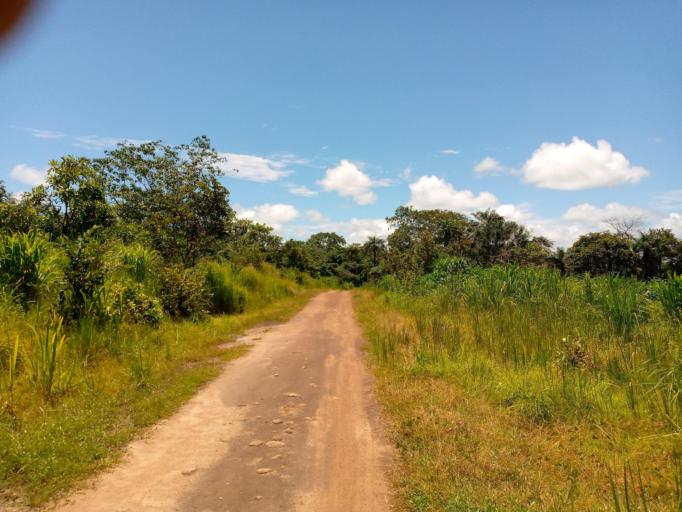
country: SL
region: Northern Province
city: Binkolo
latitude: 9.1043
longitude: -12.1404
